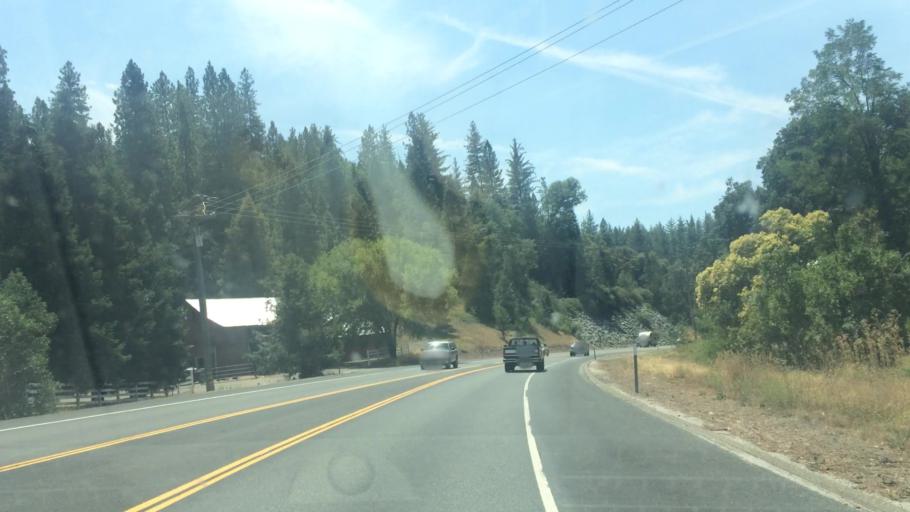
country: US
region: California
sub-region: Amador County
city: Pine Grove
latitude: 38.4030
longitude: -120.6232
